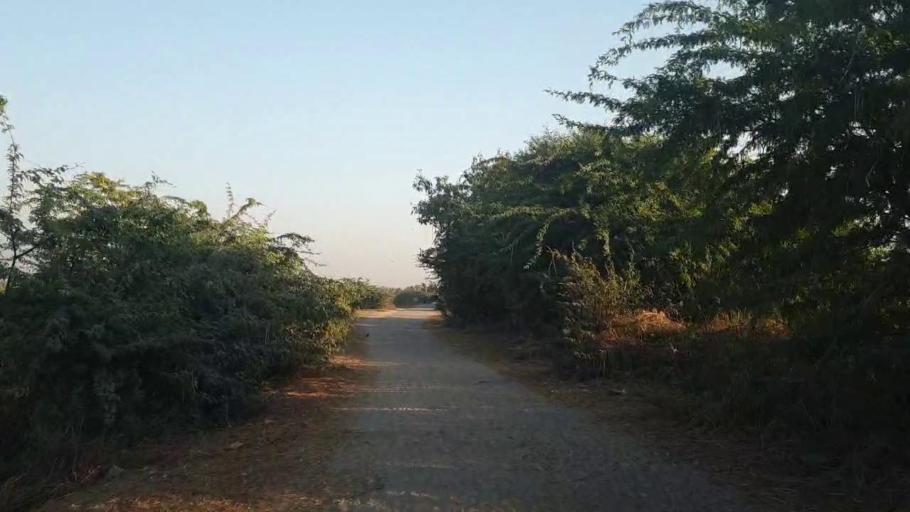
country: PK
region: Sindh
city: Mirpur Sakro
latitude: 24.4642
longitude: 67.5874
